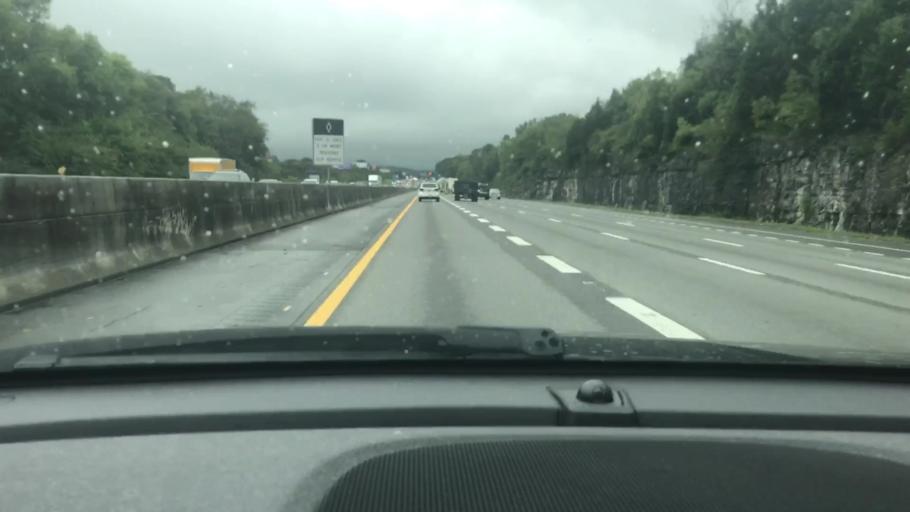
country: US
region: Tennessee
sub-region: Davidson County
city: Oak Hill
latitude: 36.0657
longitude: -86.6857
